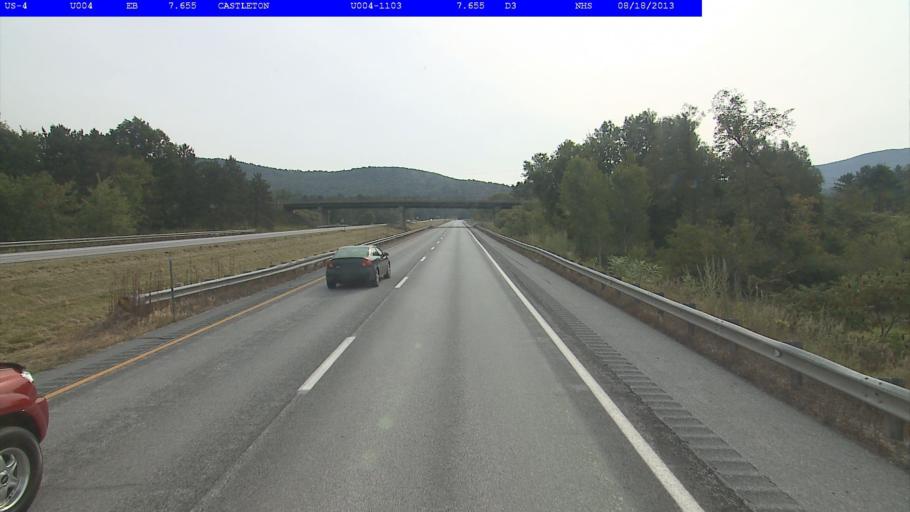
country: US
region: Vermont
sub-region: Rutland County
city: Castleton
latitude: 43.6165
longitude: -73.1677
